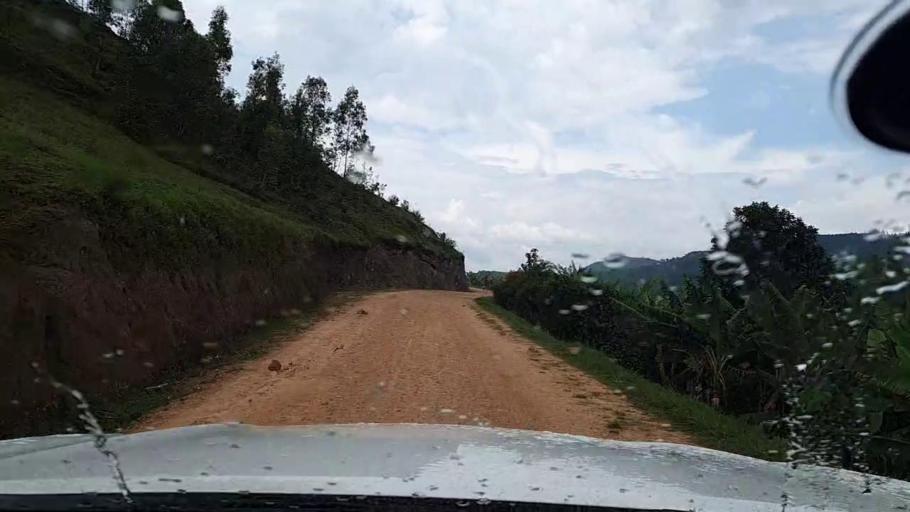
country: RW
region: Western Province
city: Kibuye
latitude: -2.1172
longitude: 29.4234
